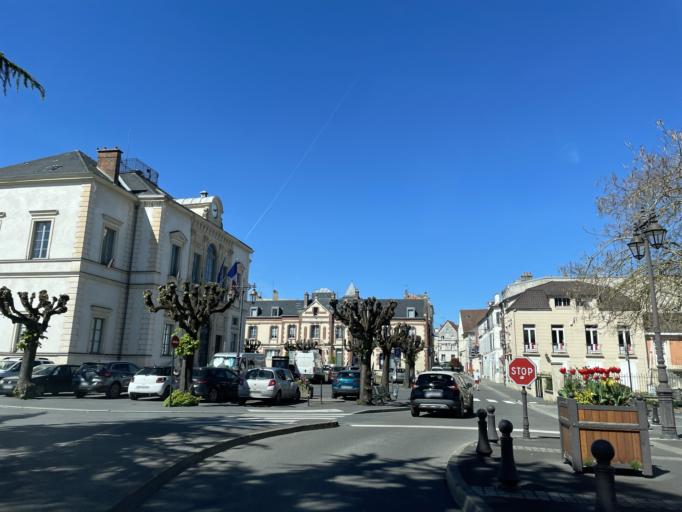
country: FR
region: Ile-de-France
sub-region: Departement de Seine-et-Marne
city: Coulommiers
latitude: 48.8118
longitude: 3.0842
